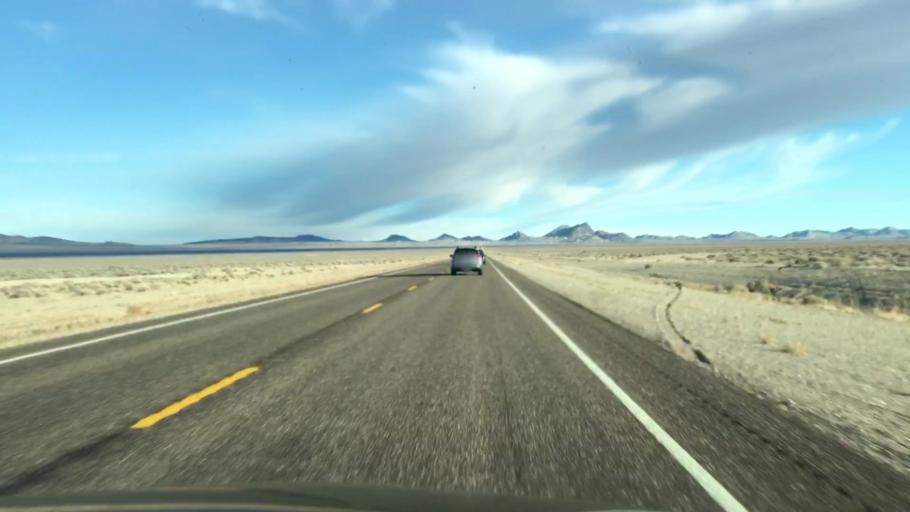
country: US
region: Nevada
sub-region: Nye County
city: Tonopah
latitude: 38.1245
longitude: -117.4051
